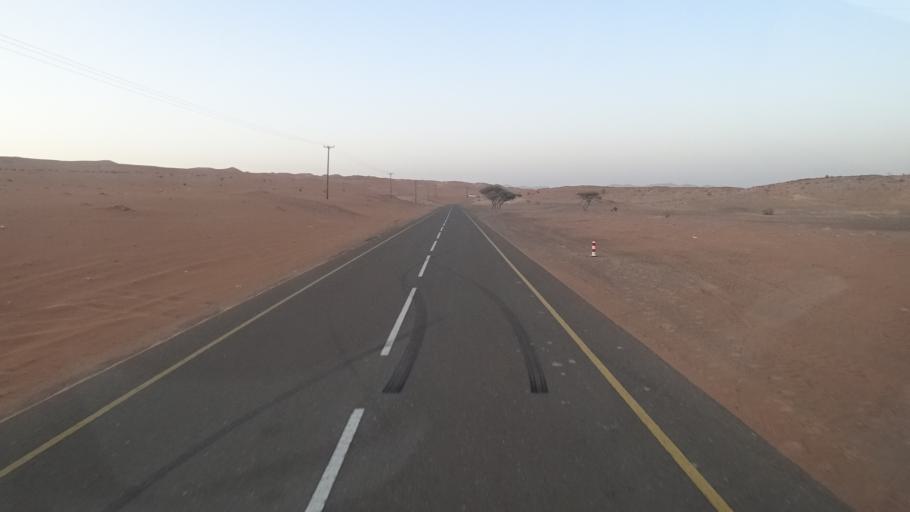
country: OM
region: Ash Sharqiyah
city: Badiyah
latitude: 22.4787
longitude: 58.7117
